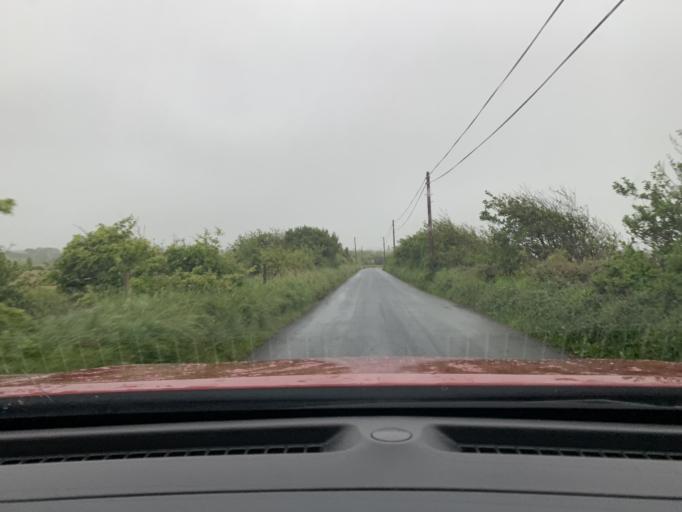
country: IE
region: Connaught
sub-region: County Leitrim
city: Kinlough
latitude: 54.4501
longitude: -8.4491
